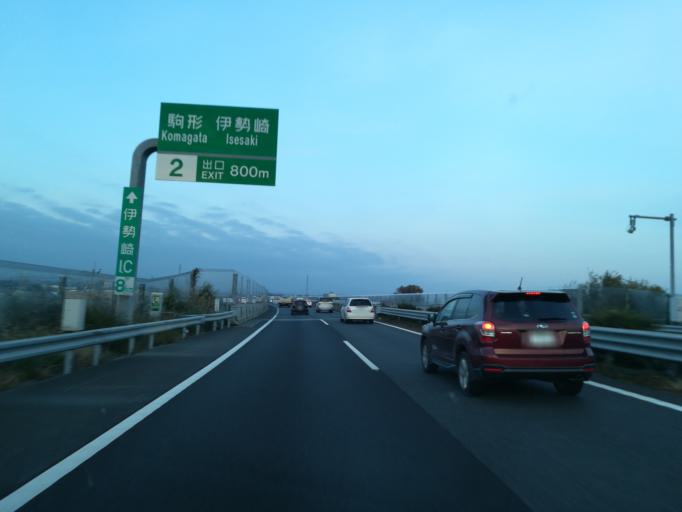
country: JP
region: Gunma
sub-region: Sawa-gun
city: Tamamura
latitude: 36.3400
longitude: 139.1353
